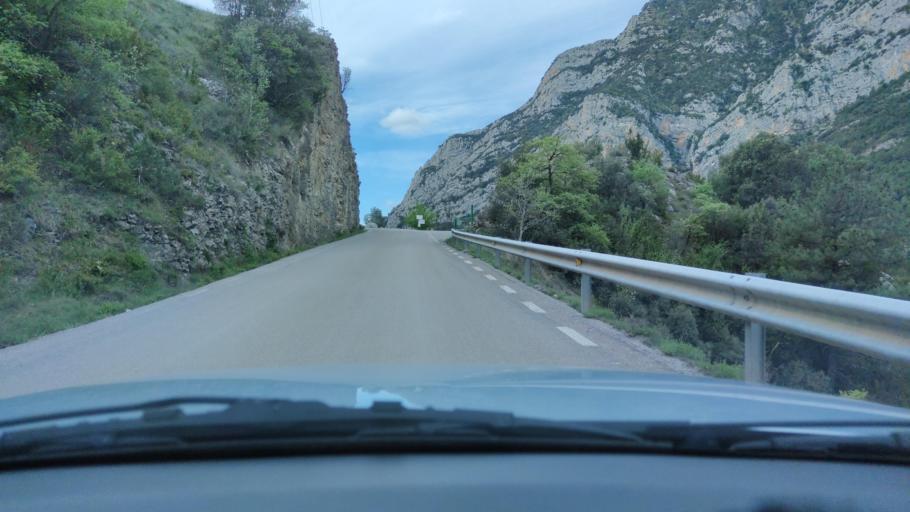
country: ES
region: Catalonia
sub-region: Provincia de Lleida
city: Coll de Nargo
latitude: 42.2463
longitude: 1.3487
